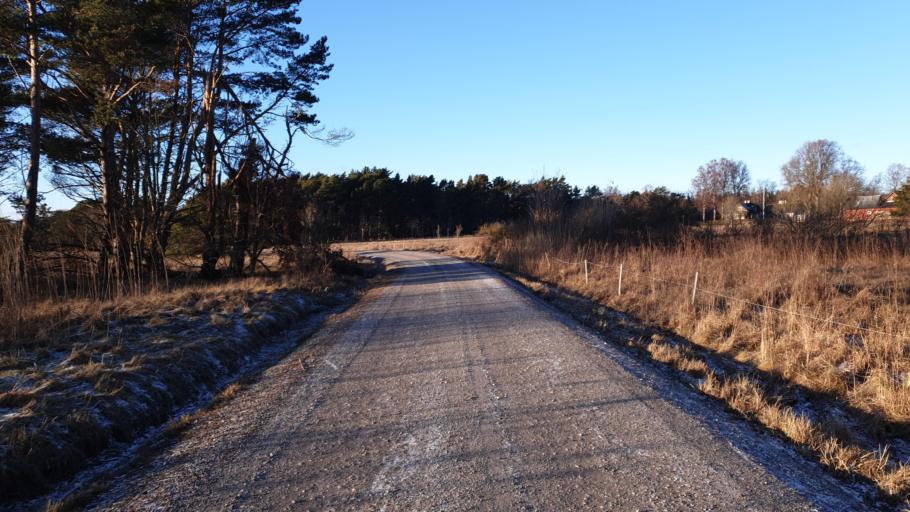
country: SE
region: Gotland
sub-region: Gotland
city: Slite
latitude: 57.3739
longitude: 18.8041
